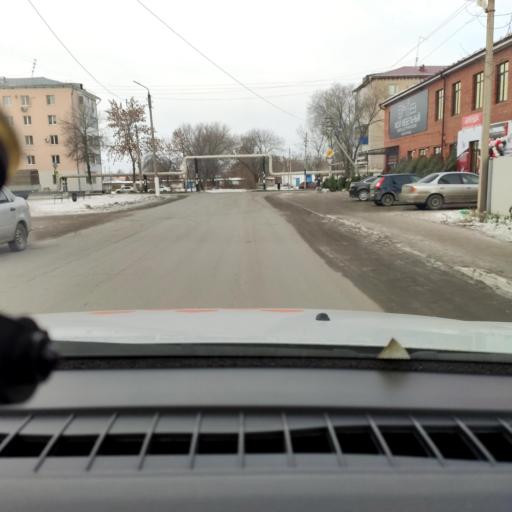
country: RU
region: Samara
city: Chapayevsk
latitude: 52.9605
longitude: 49.6874
